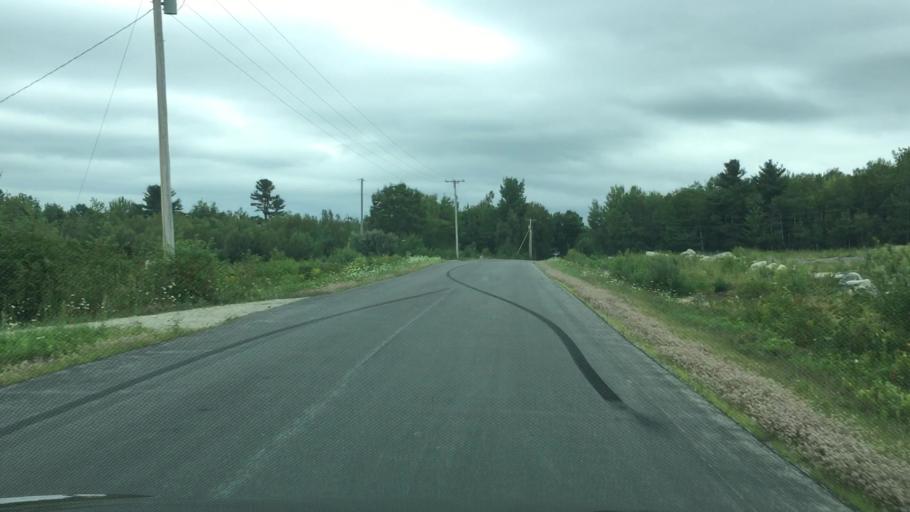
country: US
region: Maine
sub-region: Waldo County
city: Stockton Springs
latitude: 44.5271
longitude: -68.8719
